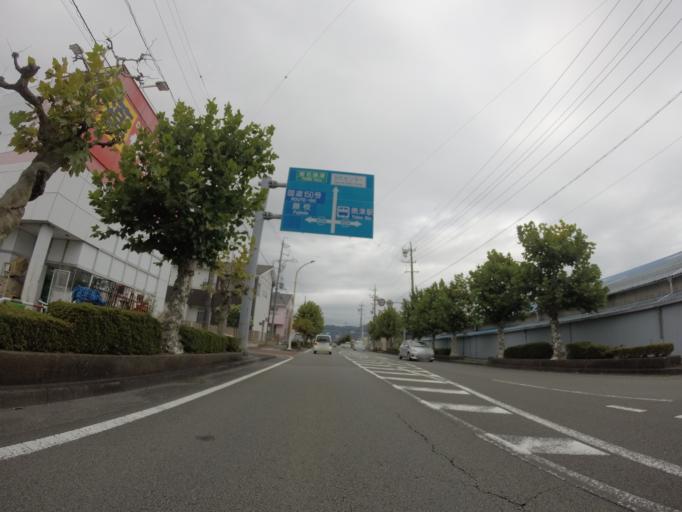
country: JP
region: Shizuoka
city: Yaizu
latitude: 34.8625
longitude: 138.3071
